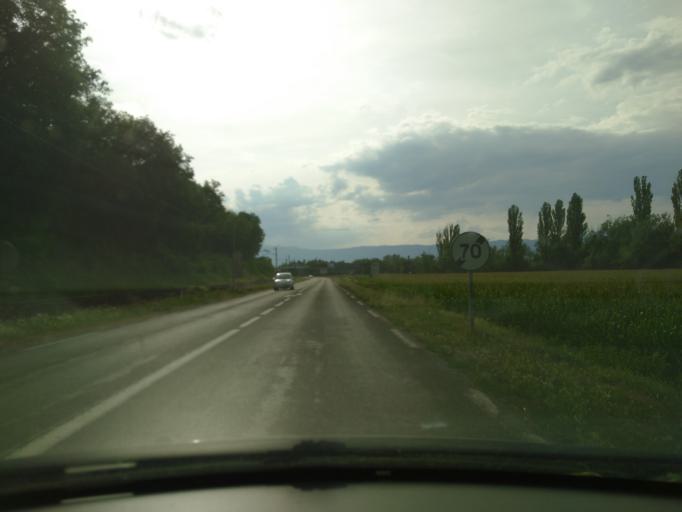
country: FR
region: Rhone-Alpes
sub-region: Departement de la Haute-Savoie
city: Neydens
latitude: 46.1430
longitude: 6.1057
